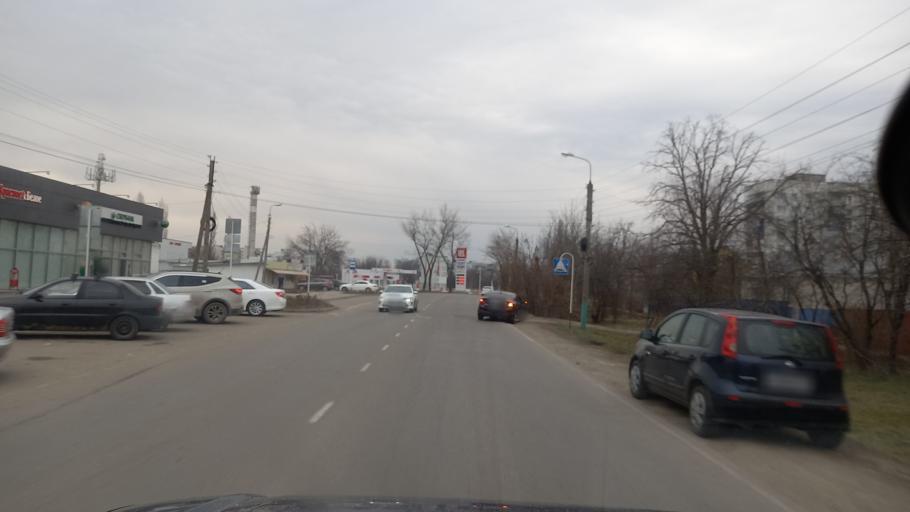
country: RU
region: Adygeya
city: Maykop
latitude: 44.5807
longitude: 40.1355
